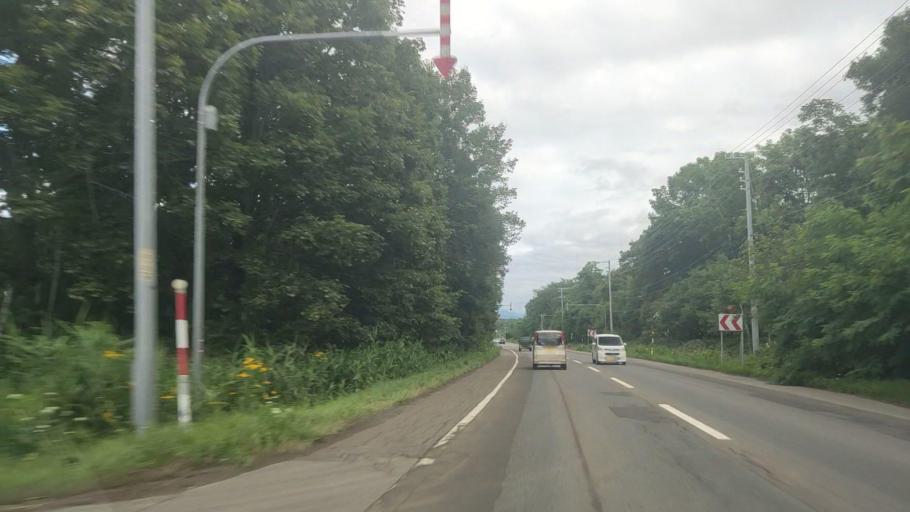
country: JP
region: Hokkaido
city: Nanae
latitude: 42.0235
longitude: 140.6140
